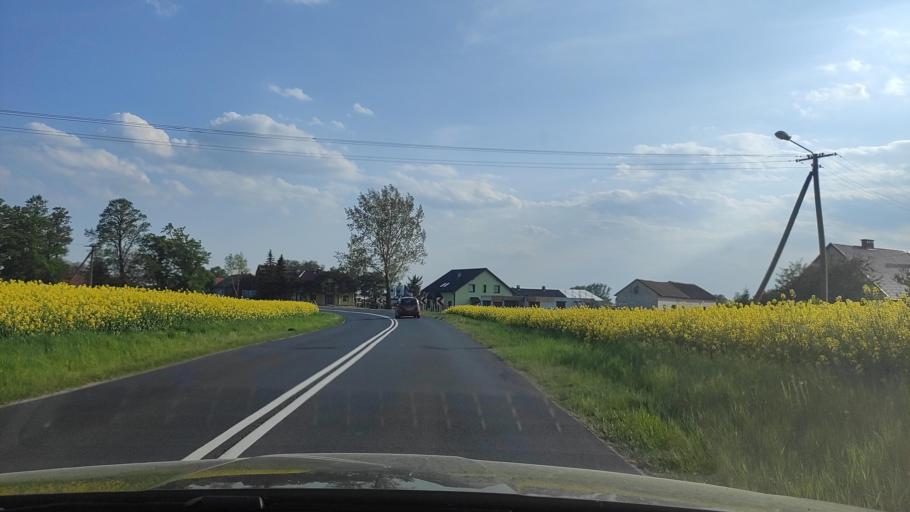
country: PL
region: Greater Poland Voivodeship
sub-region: Powiat poznanski
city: Kleszczewo
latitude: 52.3507
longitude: 17.1715
